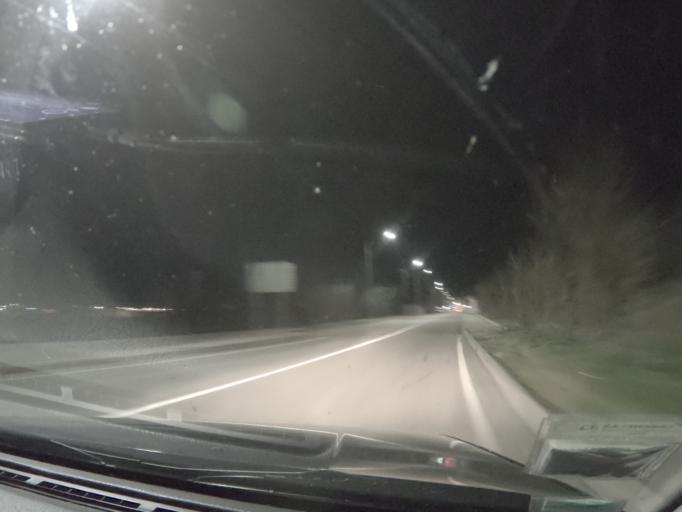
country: ES
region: Castille and Leon
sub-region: Provincia de Zamora
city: Benavente
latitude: 42.0090
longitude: -5.6698
